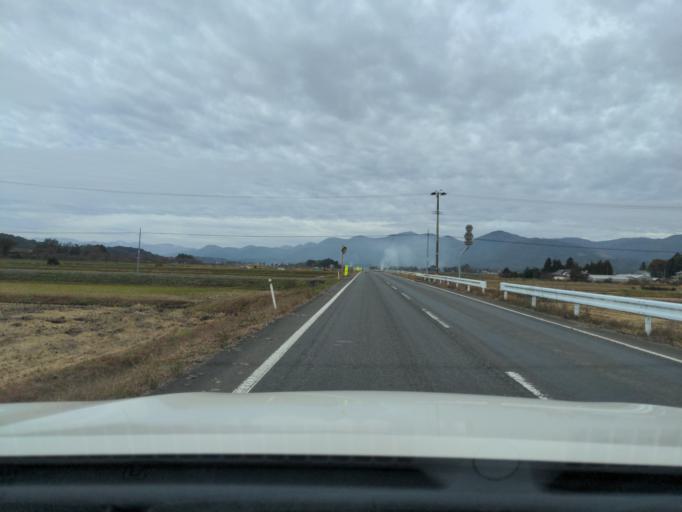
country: JP
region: Fukushima
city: Koriyama
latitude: 37.3436
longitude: 140.2892
